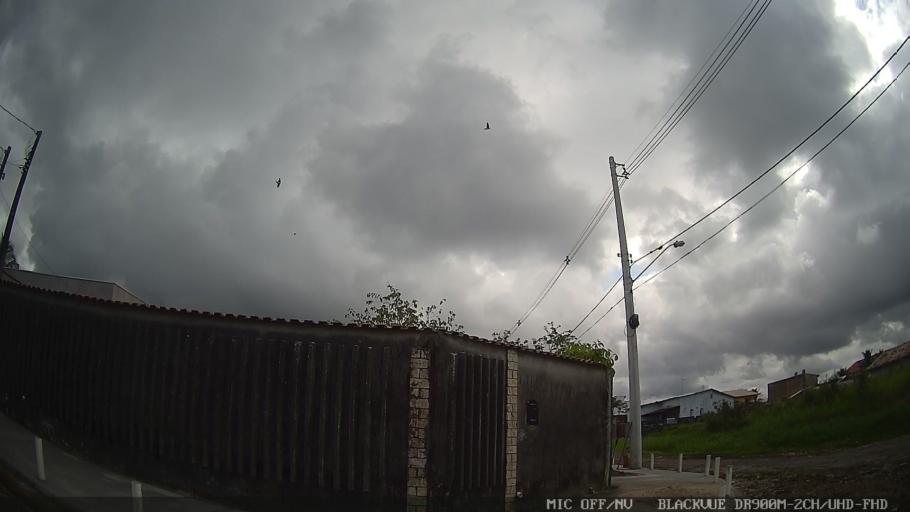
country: BR
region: Sao Paulo
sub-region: Itanhaem
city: Itanhaem
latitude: -24.2036
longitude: -46.8441
